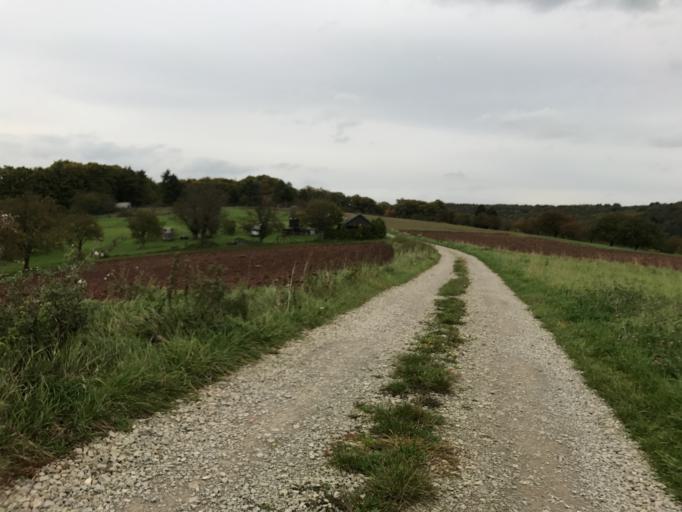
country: DE
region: Hesse
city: Witzenhausen
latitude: 51.3000
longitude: 9.8450
